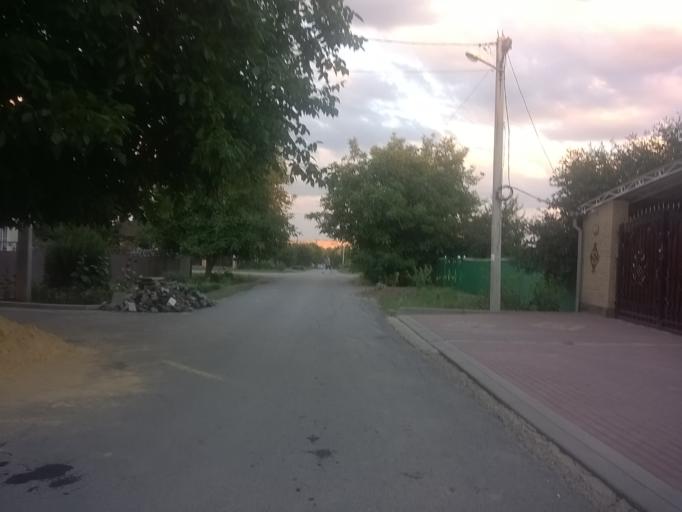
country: RU
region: Rostov
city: Donetsk
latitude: 48.3344
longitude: 39.9549
